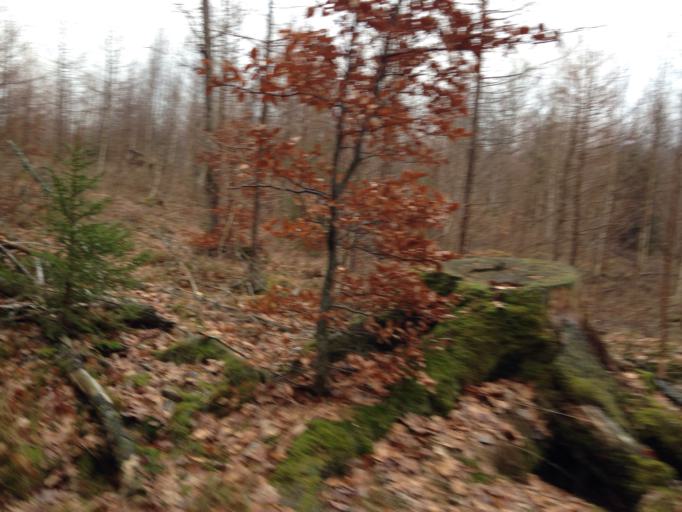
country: SE
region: Joenkoeping
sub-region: Varnamo Kommun
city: Bor
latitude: 57.0365
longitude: 14.1849
